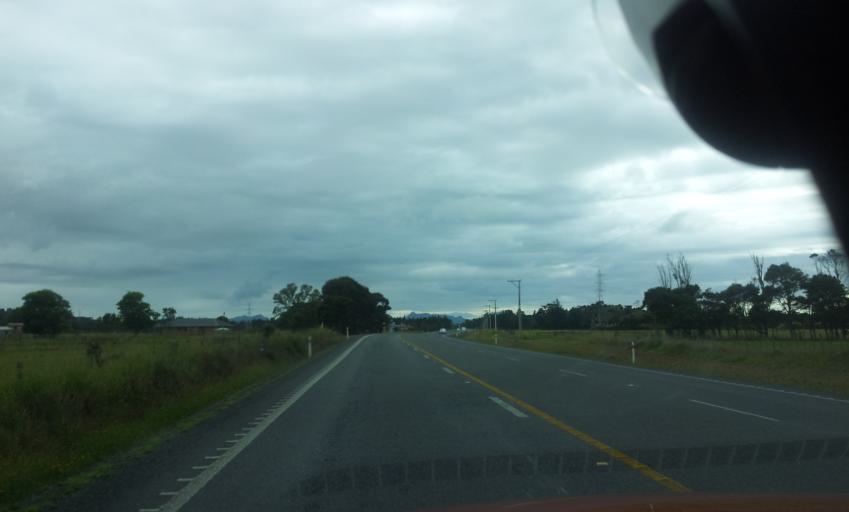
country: NZ
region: Northland
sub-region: Whangarei
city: Ruakaka
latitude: -35.9945
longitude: 174.4204
